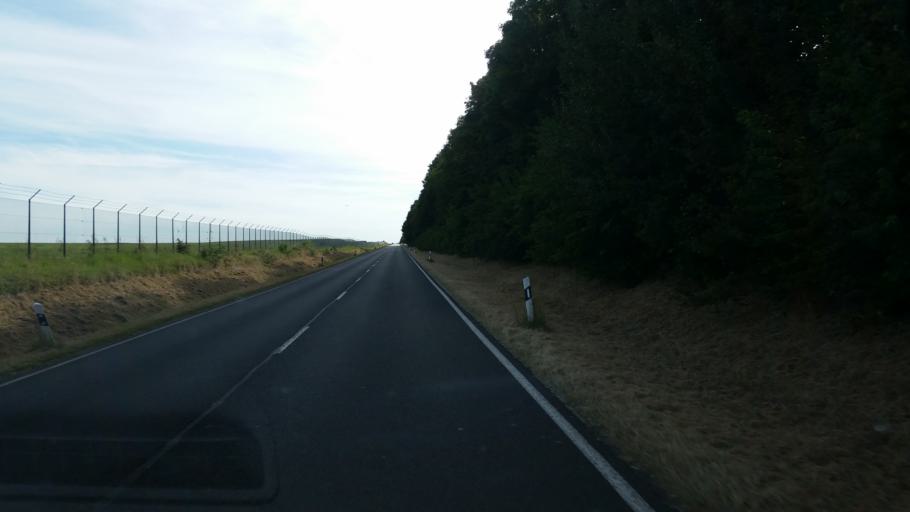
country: DE
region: Rheinland-Pfalz
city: Hahn
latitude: 49.9560
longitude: 7.2669
